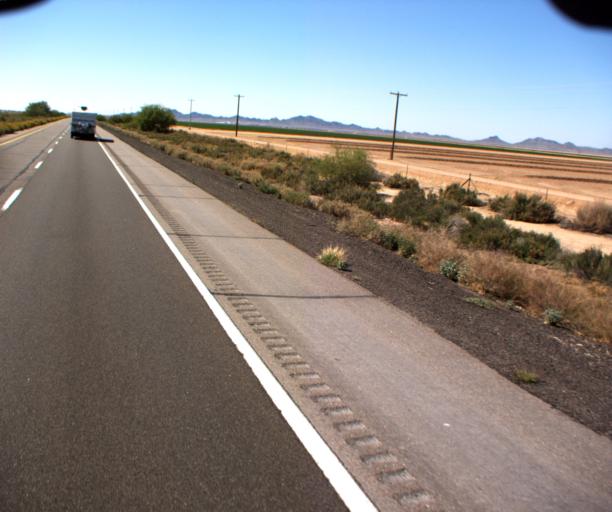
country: US
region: Arizona
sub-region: Maricopa County
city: Gila Bend
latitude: 32.9169
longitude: -112.9195
